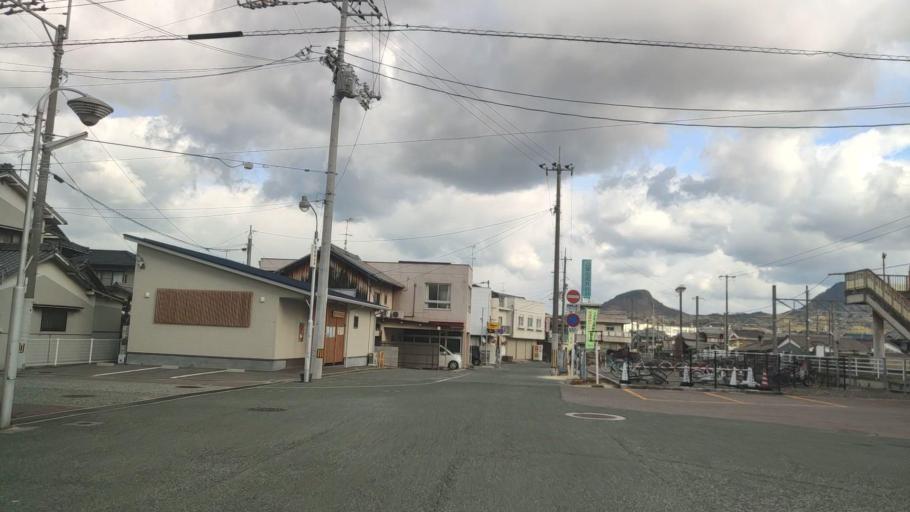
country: JP
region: Ehime
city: Hojo
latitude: 33.9725
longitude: 132.7749
